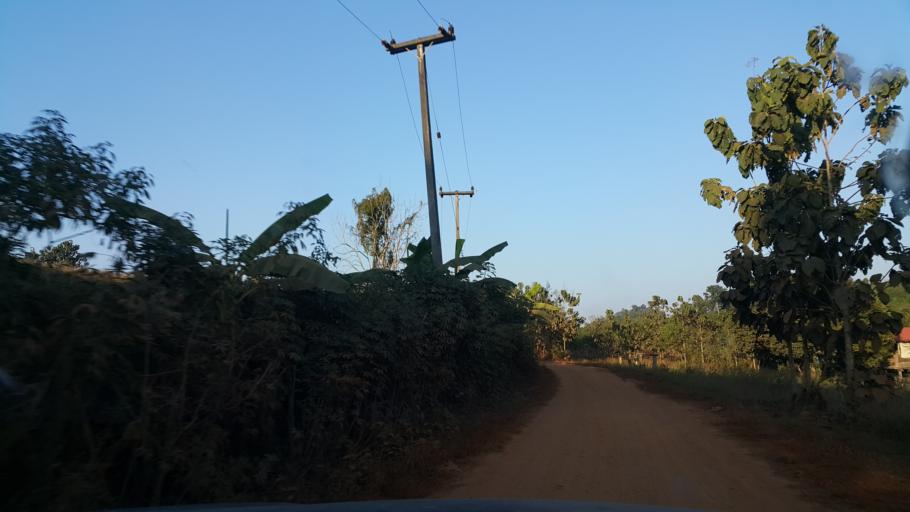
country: TH
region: Sukhothai
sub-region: Amphoe Si Satchanalai
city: Si Satchanalai
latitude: 17.6130
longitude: 99.6218
